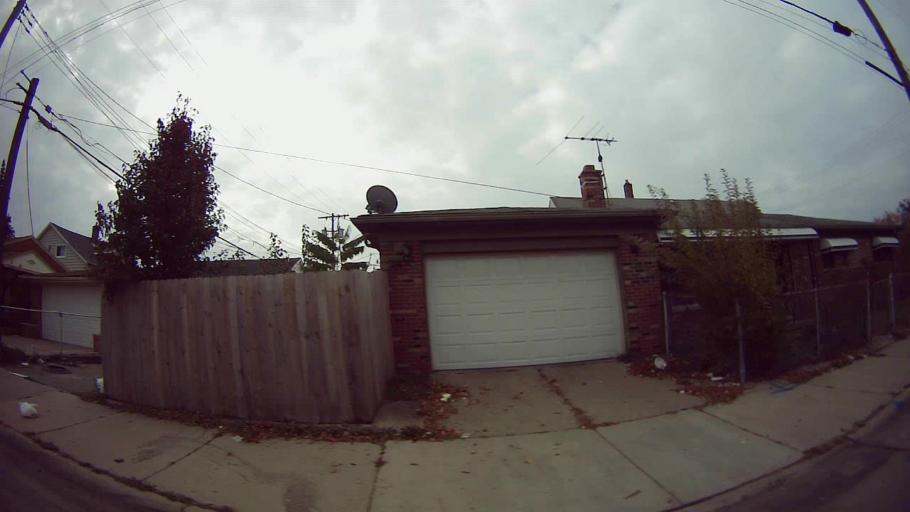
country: US
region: Michigan
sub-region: Wayne County
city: Hamtramck
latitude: 42.4051
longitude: -83.0666
